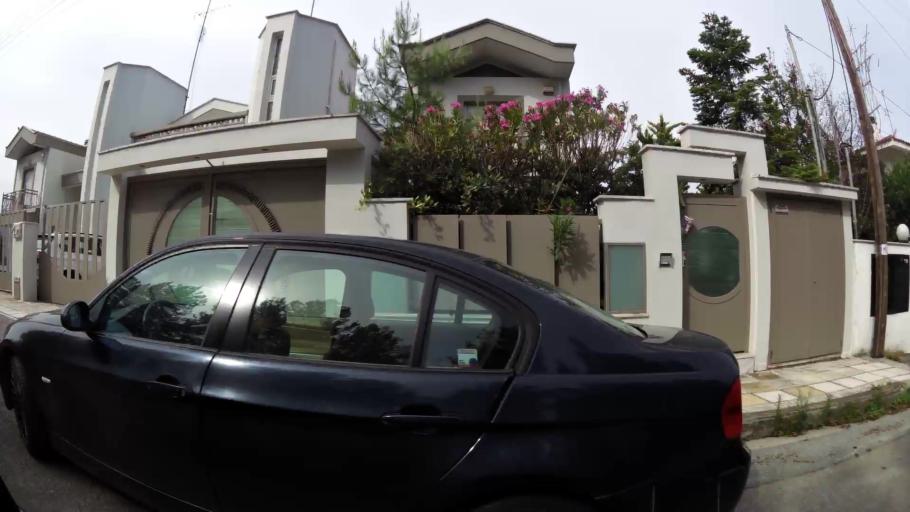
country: GR
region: Central Macedonia
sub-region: Nomos Thessalonikis
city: Panorama
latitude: 40.5873
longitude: 23.0266
